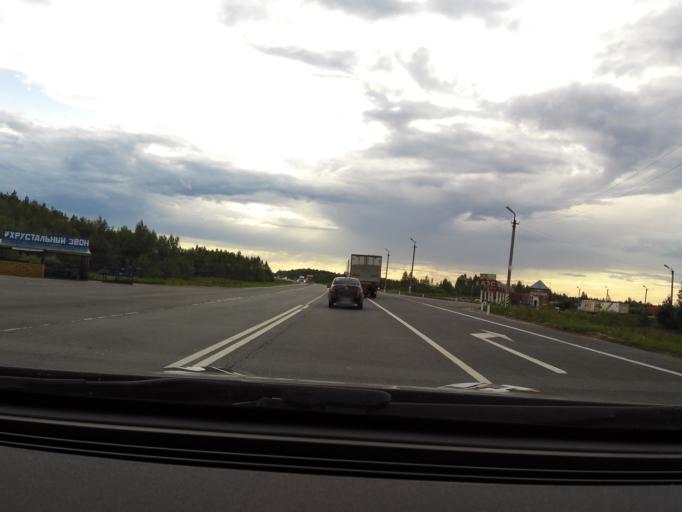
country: RU
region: Vladimir
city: Raduzhnyy
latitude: 56.0718
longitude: 40.2813
